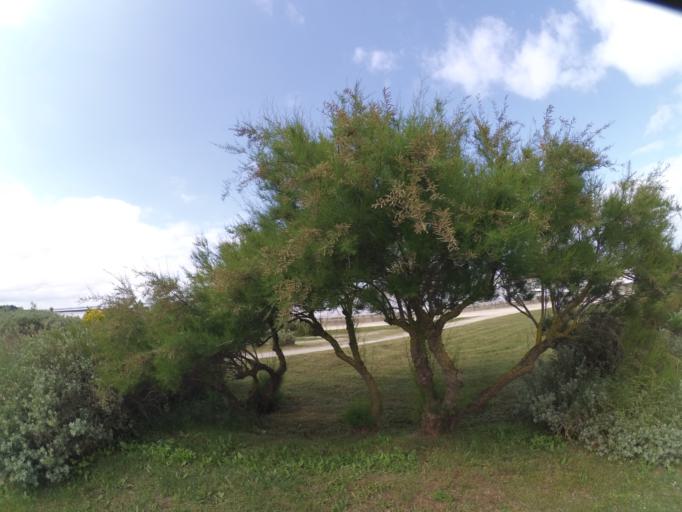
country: FR
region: Poitou-Charentes
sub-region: Departement de la Charente-Maritime
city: Chatelaillon-Plage
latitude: 46.0611
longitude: -1.0909
